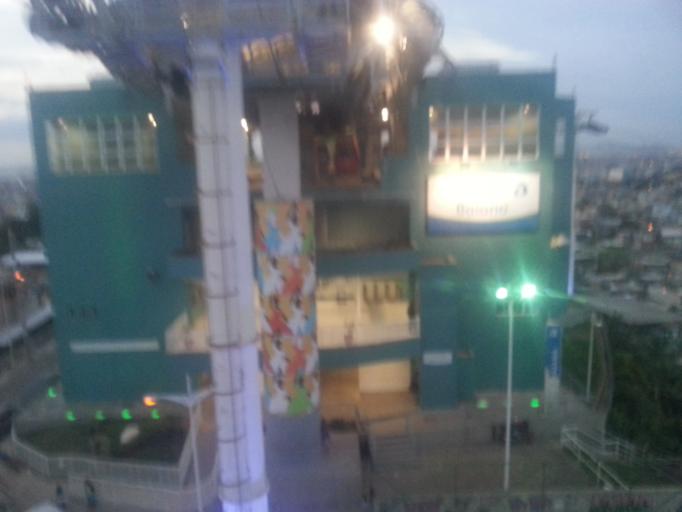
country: BR
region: Rio de Janeiro
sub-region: Rio De Janeiro
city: Rio de Janeiro
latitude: -22.8584
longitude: -43.2667
